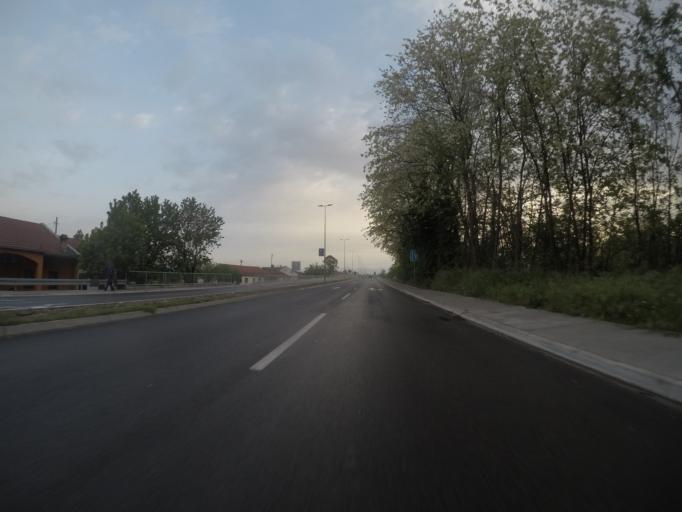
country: ME
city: Mojanovici
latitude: 42.3449
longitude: 19.2220
